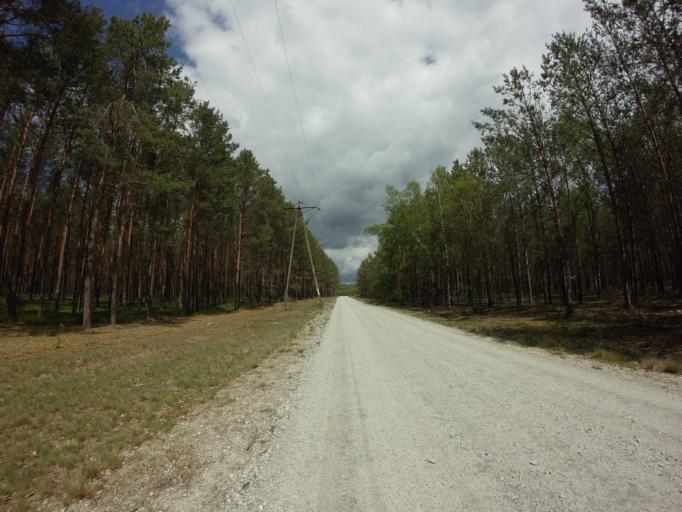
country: PL
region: West Pomeranian Voivodeship
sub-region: Powiat drawski
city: Kalisz Pomorski
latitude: 53.1905
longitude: 15.9734
